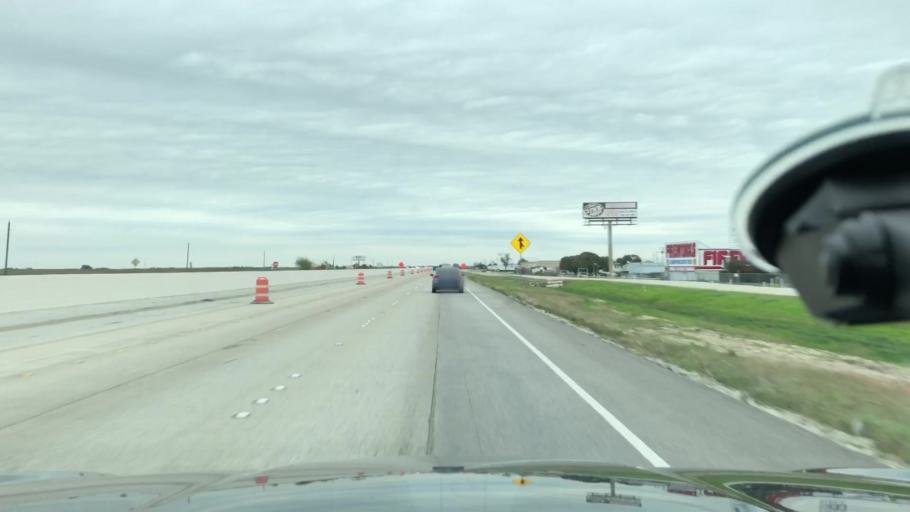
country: US
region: Texas
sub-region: Ellis County
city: Oak Leaf
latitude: 32.4757
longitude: -96.8353
